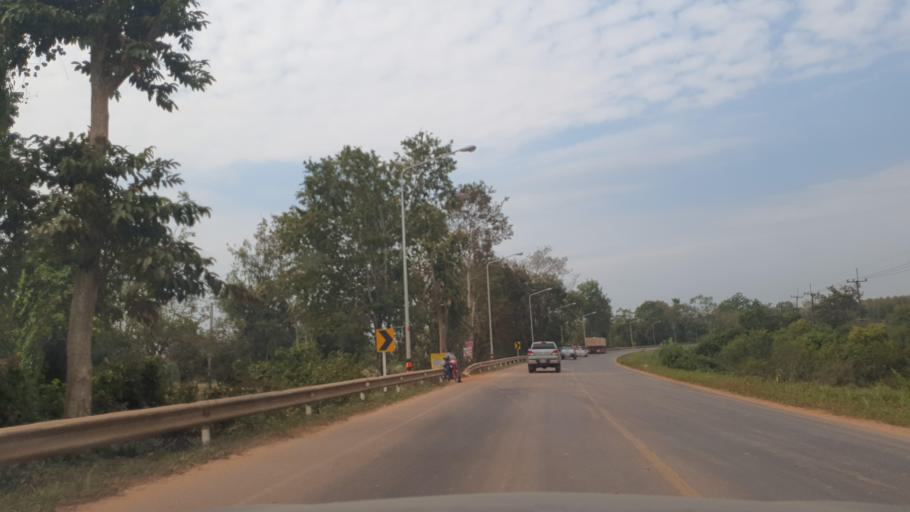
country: TH
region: Changwat Bueng Kan
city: Si Wilai
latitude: 18.2723
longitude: 103.8356
